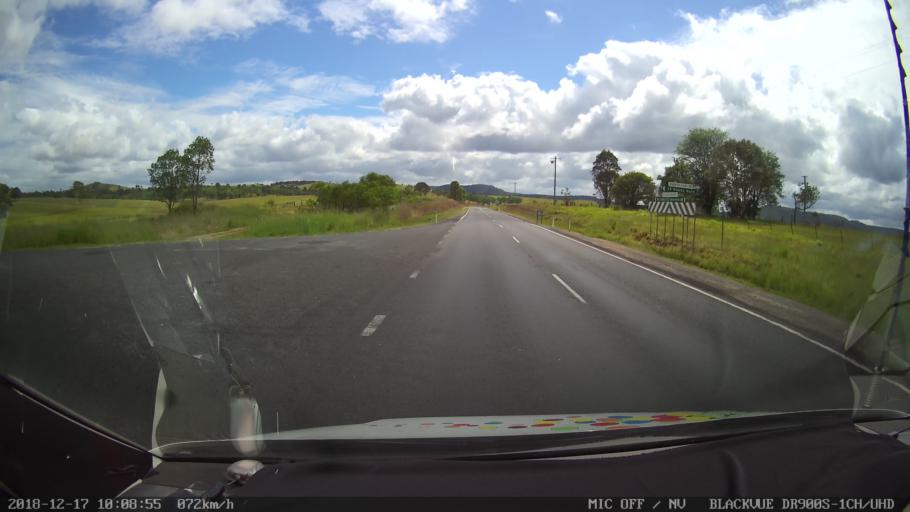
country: AU
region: New South Wales
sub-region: Tenterfield Municipality
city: Carrolls Creek
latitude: -28.8891
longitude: 152.5375
